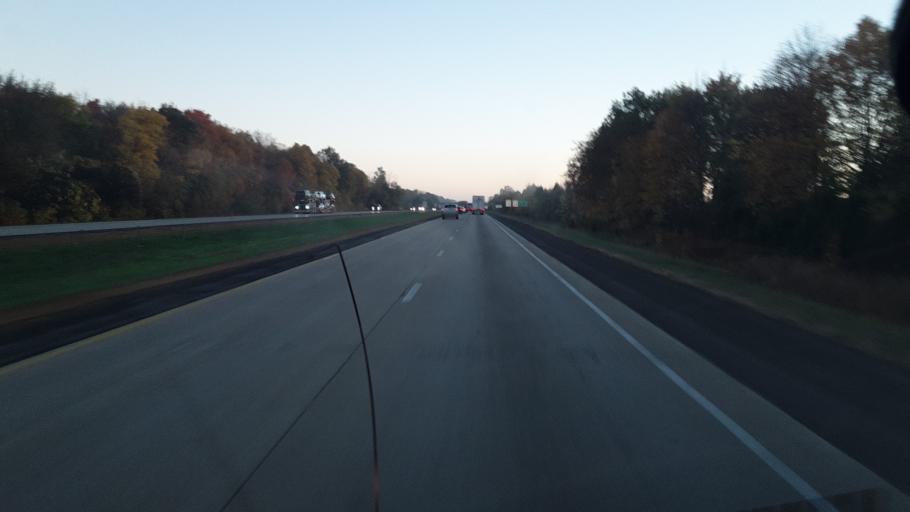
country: US
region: Indiana
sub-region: DeKalb County
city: Auburn
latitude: 41.3739
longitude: -85.0777
